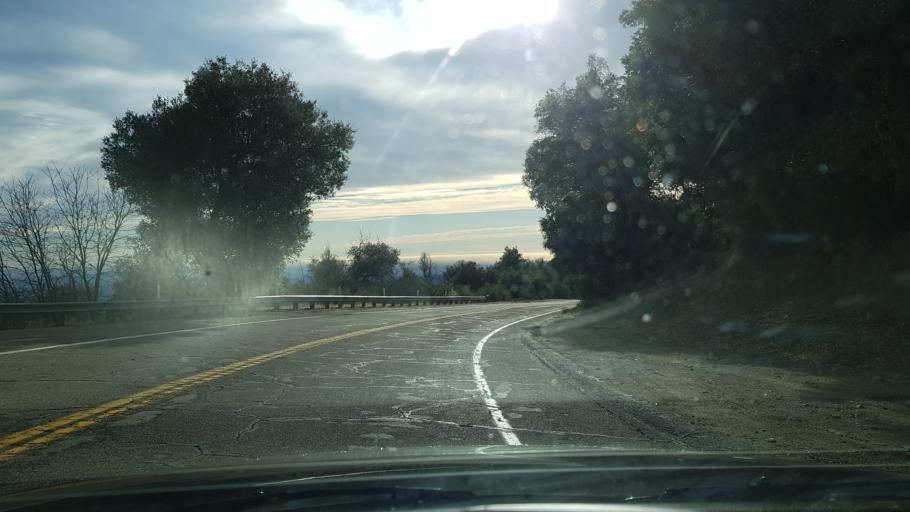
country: US
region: California
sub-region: Riverside County
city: Aguanga
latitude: 33.3105
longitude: -116.8707
